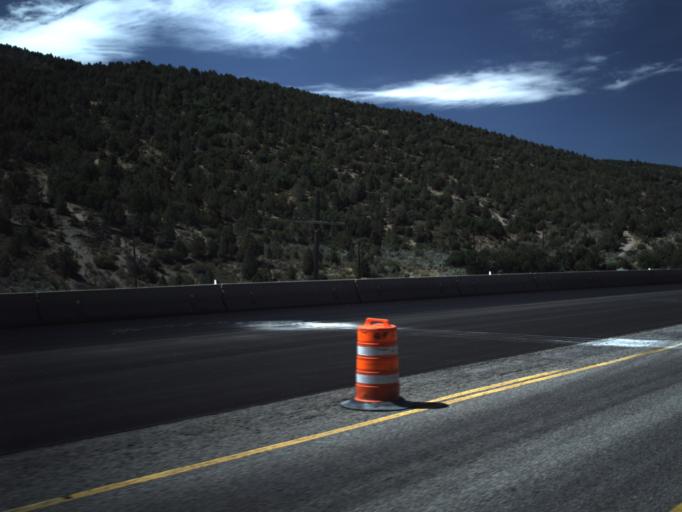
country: US
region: Utah
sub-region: Utah County
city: Mapleton
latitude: 39.9519
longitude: -111.2729
